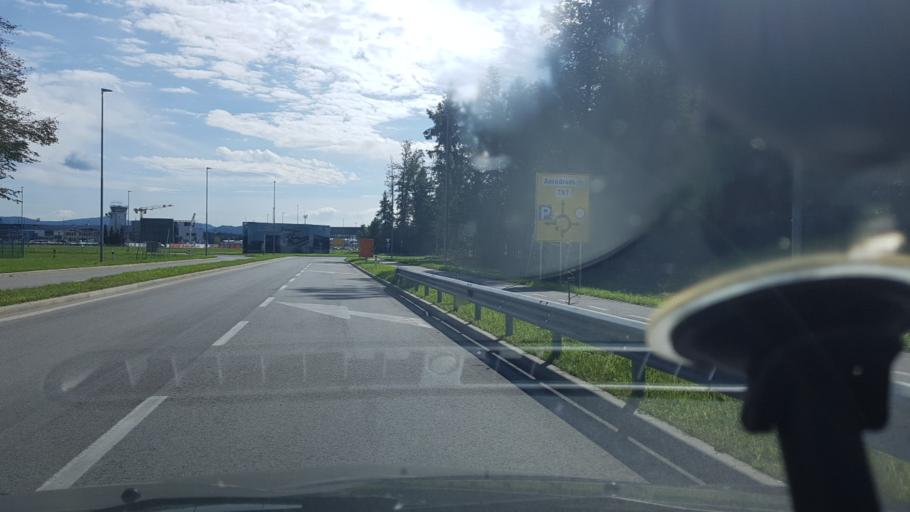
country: SI
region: Sencur
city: Sencur
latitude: 46.2354
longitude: 14.4514
